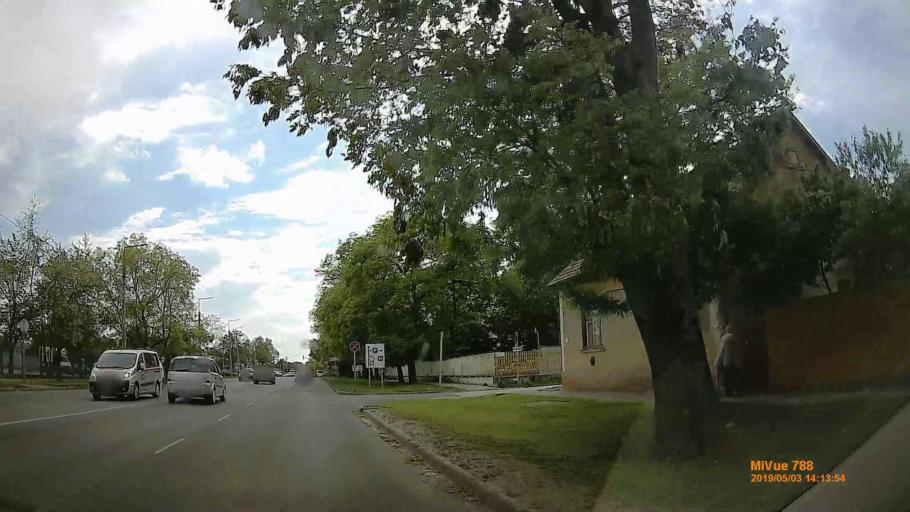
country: HU
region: Jasz-Nagykun-Szolnok
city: Szolnok
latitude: 47.1583
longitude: 20.1728
